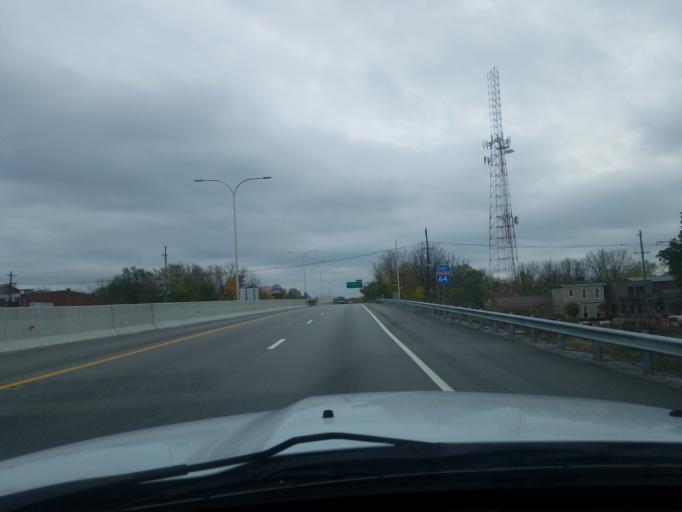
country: US
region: Indiana
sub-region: Clark County
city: Jeffersonville
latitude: 38.2589
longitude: -85.7238
